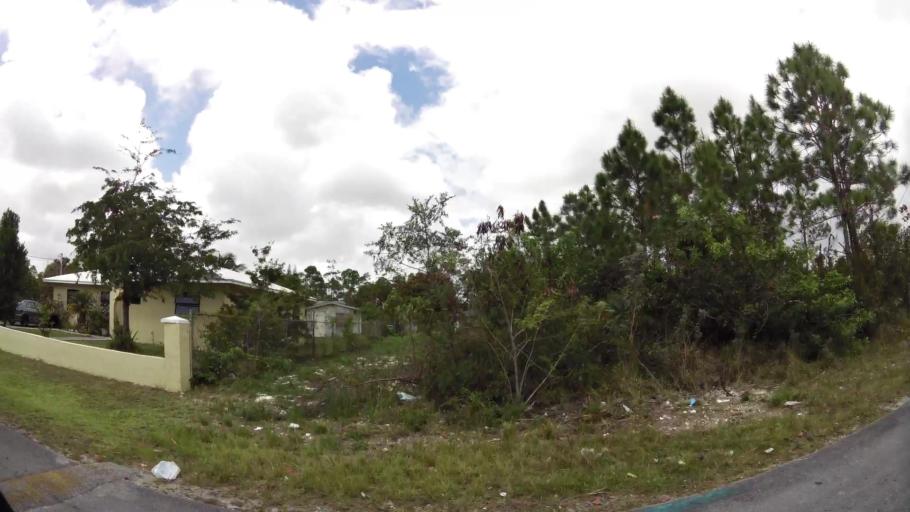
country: BS
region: Freeport
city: Lucaya
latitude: 26.5454
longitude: -78.6433
